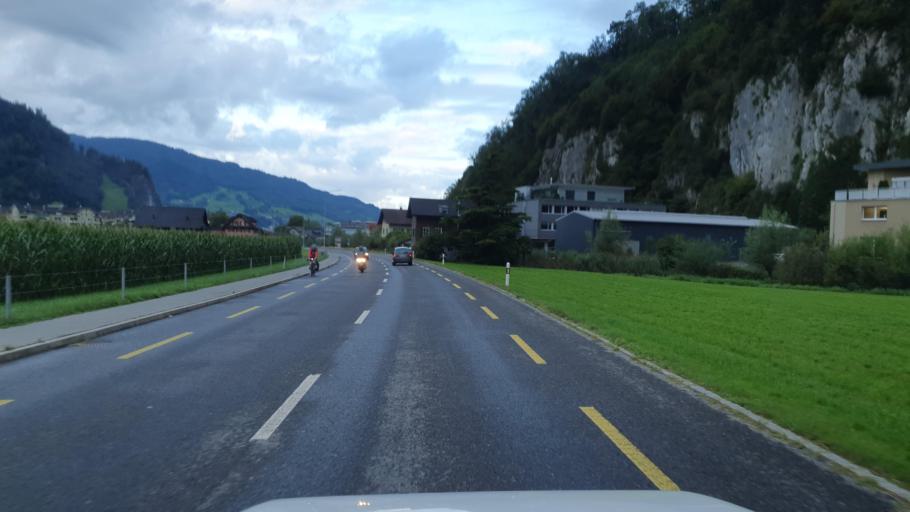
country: CH
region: Nidwalden
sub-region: Nidwalden
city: Stansstad
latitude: 46.9723
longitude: 8.3484
